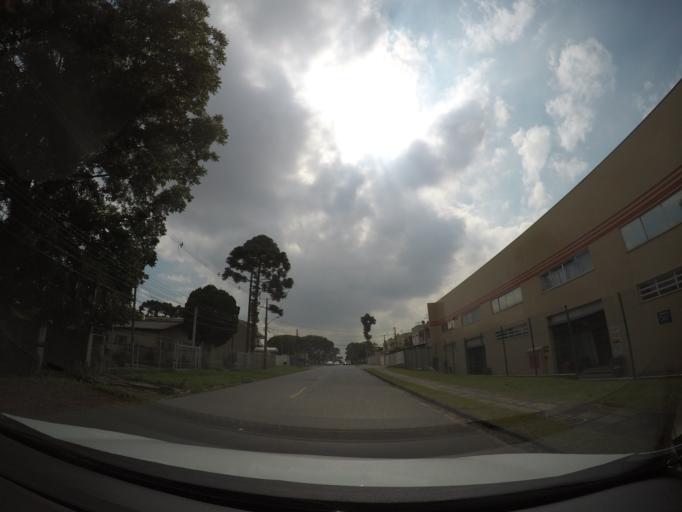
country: BR
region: Parana
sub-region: Sao Jose Dos Pinhais
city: Sao Jose dos Pinhais
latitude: -25.5035
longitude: -49.2392
